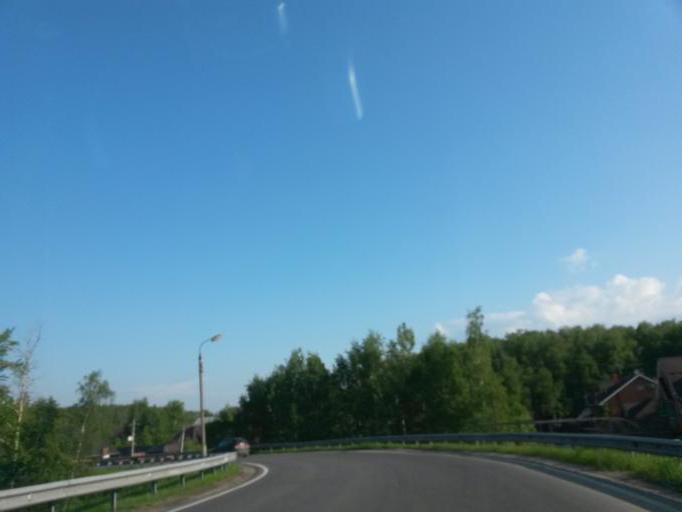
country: RU
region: Moskovskaya
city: Gorki-Leninskiye
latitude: 55.5137
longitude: 37.8310
